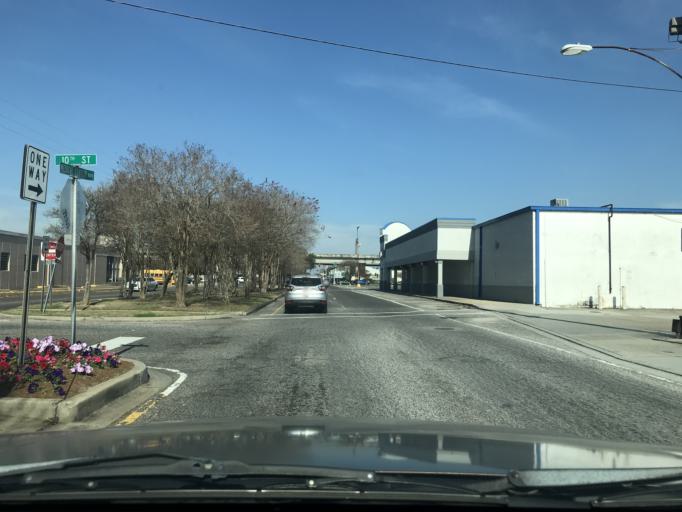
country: US
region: Louisiana
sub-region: Jefferson Parish
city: Marrero
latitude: 29.8932
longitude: -90.0961
